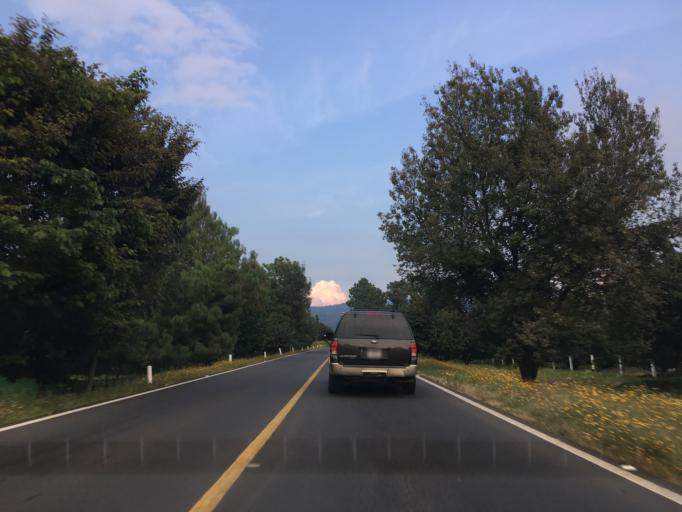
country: MX
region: Michoacan
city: Tingambato
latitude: 19.4986
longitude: -101.8715
